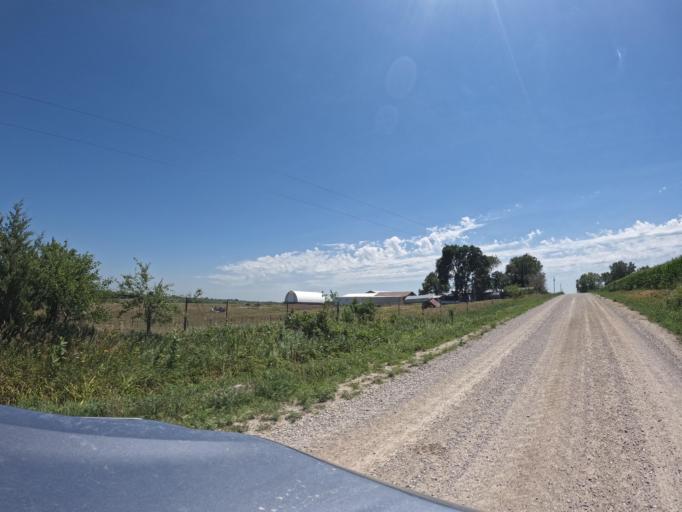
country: US
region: Iowa
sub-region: Keokuk County
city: Sigourney
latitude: 41.4163
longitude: -92.3164
